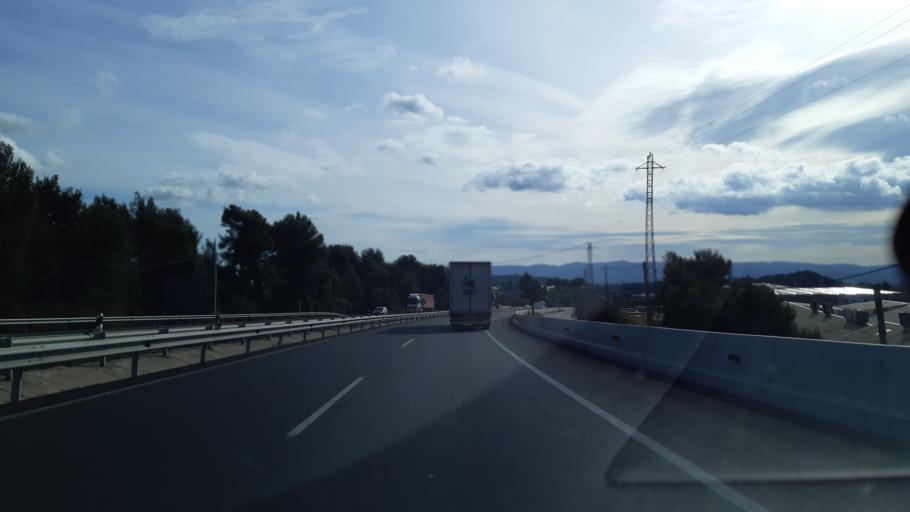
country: ES
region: Catalonia
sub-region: Provincia de Barcelona
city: Collbato
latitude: 41.5826
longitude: 1.7765
